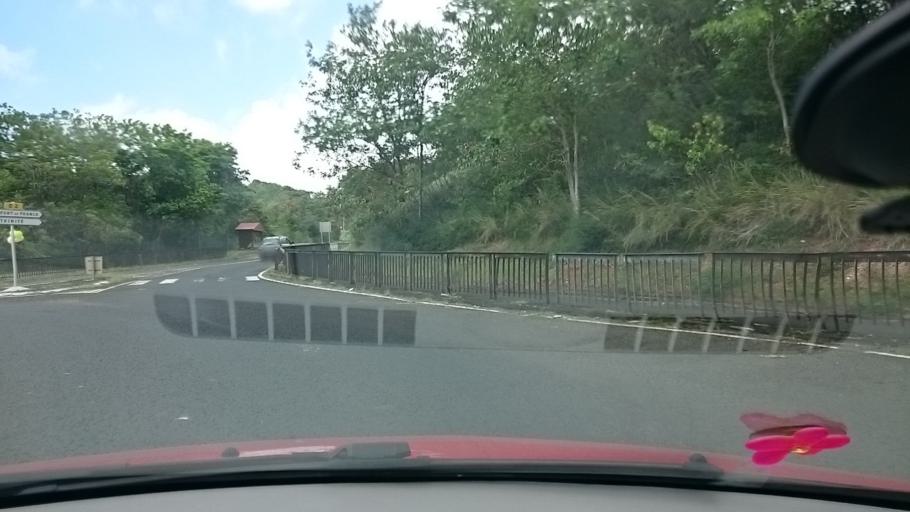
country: MQ
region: Martinique
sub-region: Martinique
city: La Trinite
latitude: 14.7424
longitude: -60.9477
